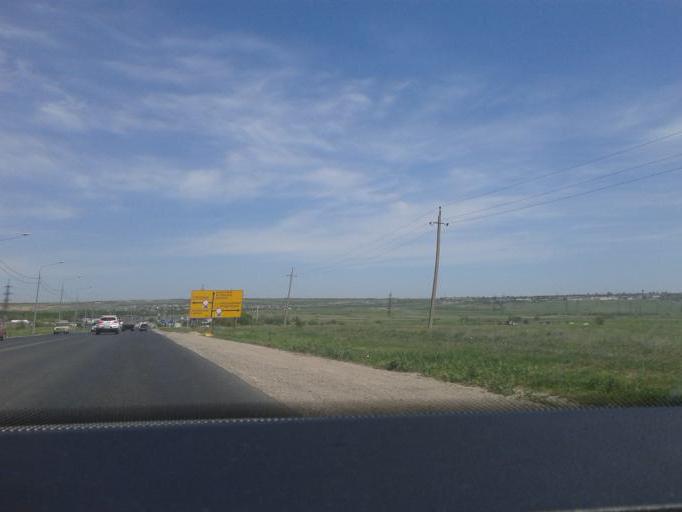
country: RU
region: Volgograd
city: Vodstroy
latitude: 48.8168
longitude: 44.5249
